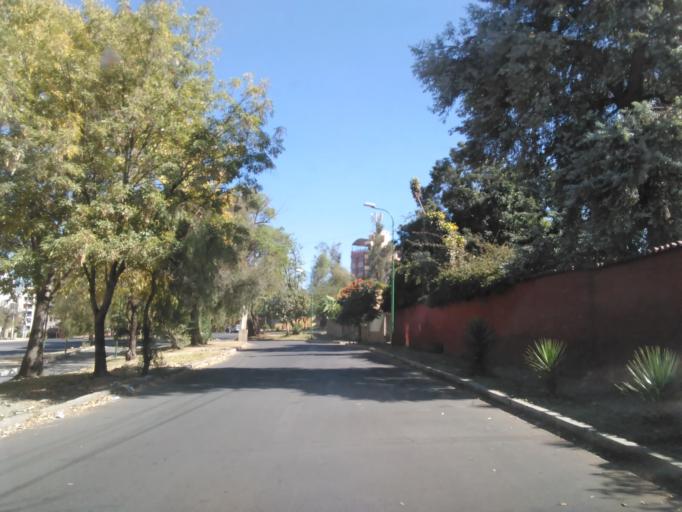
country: BO
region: Cochabamba
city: Cochabamba
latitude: -17.3692
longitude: -66.1579
